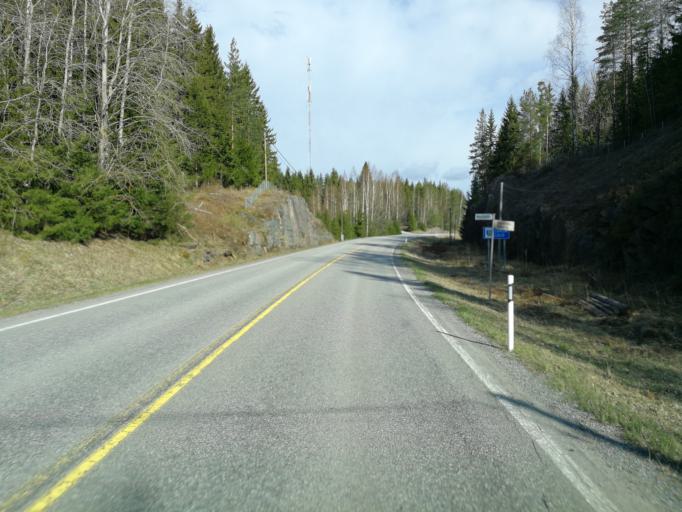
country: FI
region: Uusimaa
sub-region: Helsinki
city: Karjalohja
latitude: 60.1776
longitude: 23.7638
